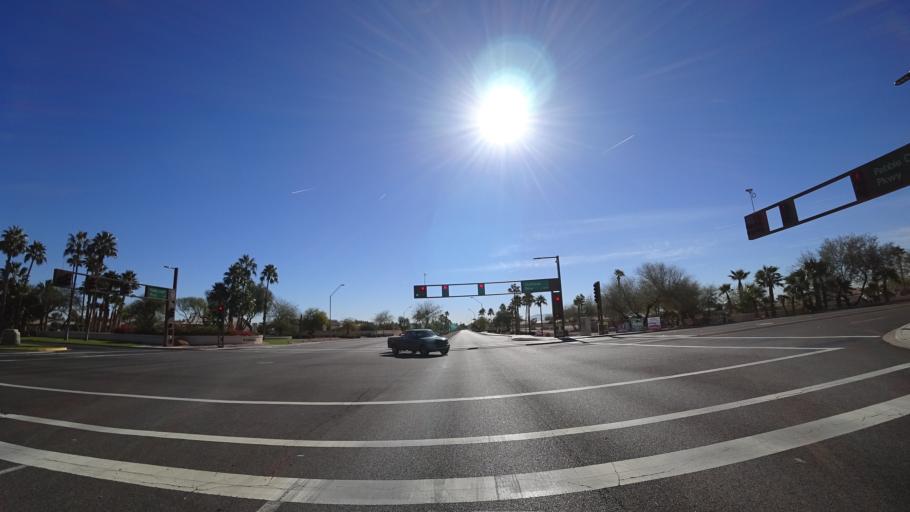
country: US
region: Arizona
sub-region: Maricopa County
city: Litchfield Park
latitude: 33.4872
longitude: -112.3977
